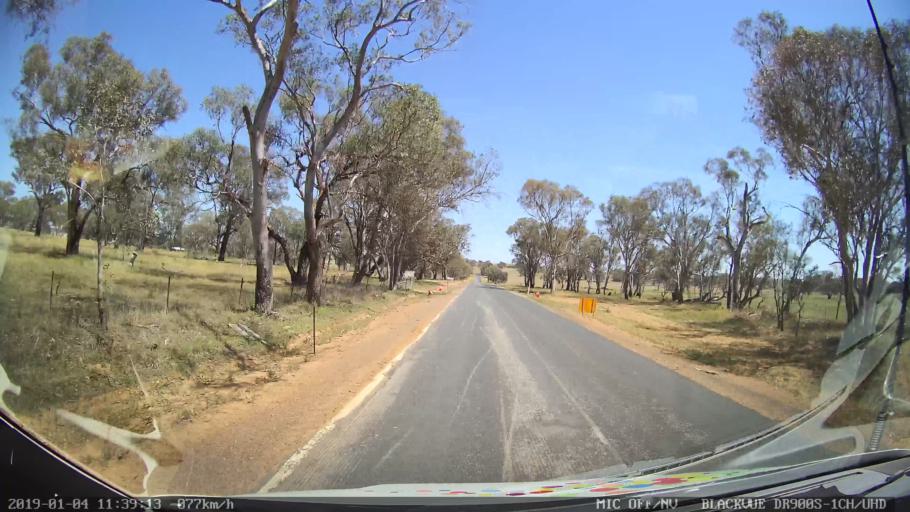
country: AU
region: New South Wales
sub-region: Cabonne
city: Molong
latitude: -33.0154
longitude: 148.7976
